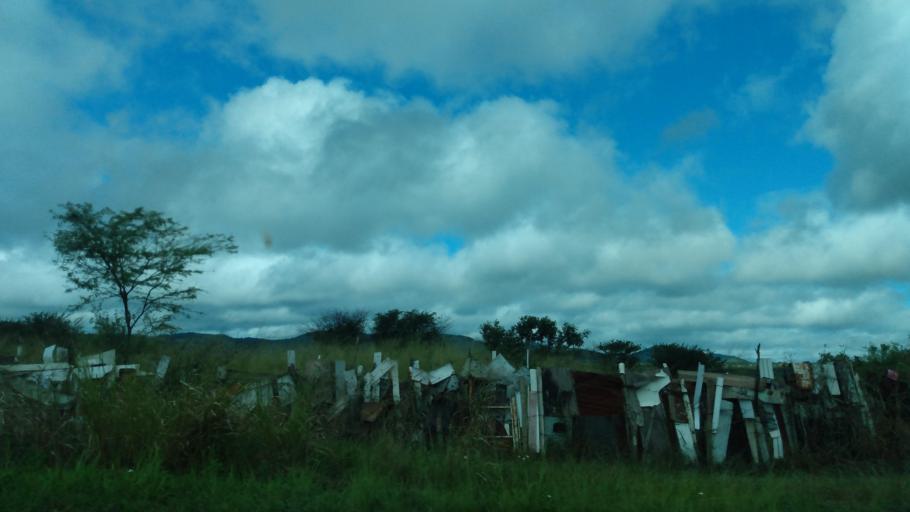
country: BR
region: Pernambuco
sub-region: Caruaru
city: Caruaru
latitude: -8.3224
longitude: -35.9902
